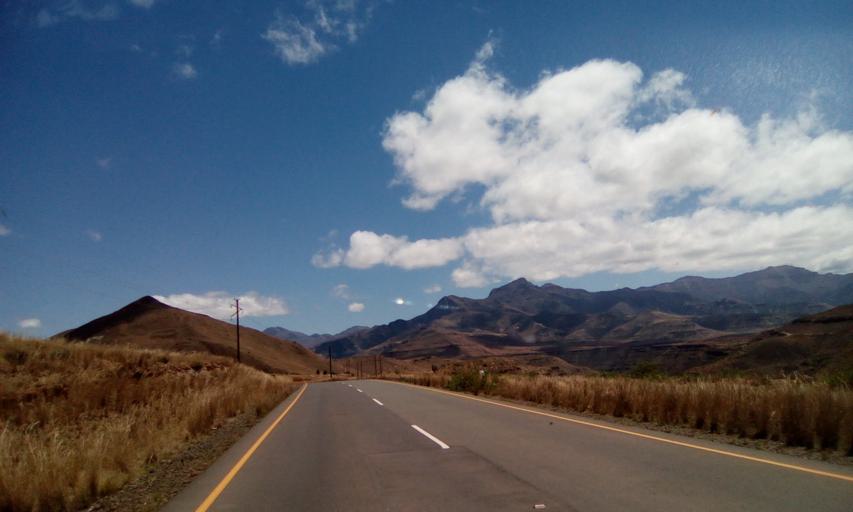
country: LS
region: Qacha's Nek
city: Qacha's Nek
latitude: -30.0826
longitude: 28.6295
